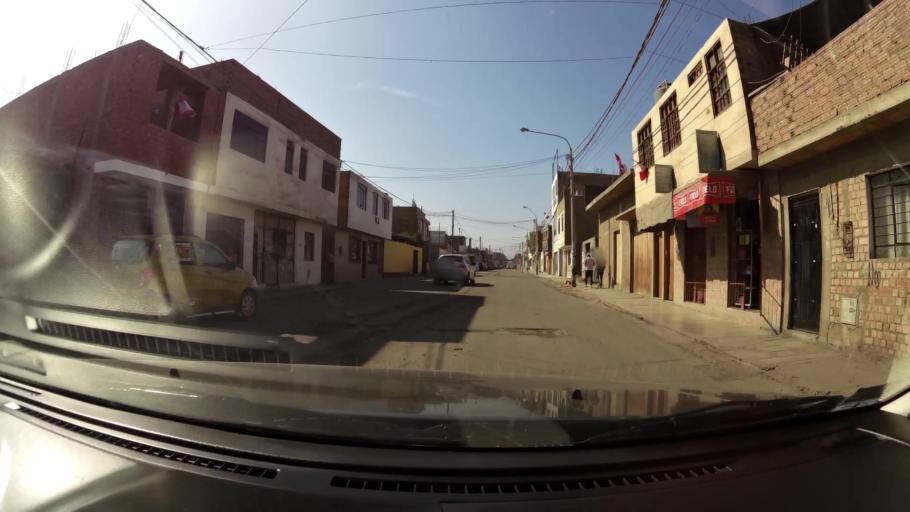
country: PE
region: Ica
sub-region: Provincia de Chincha
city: Chincha Alta
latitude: -13.4239
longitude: -76.1339
